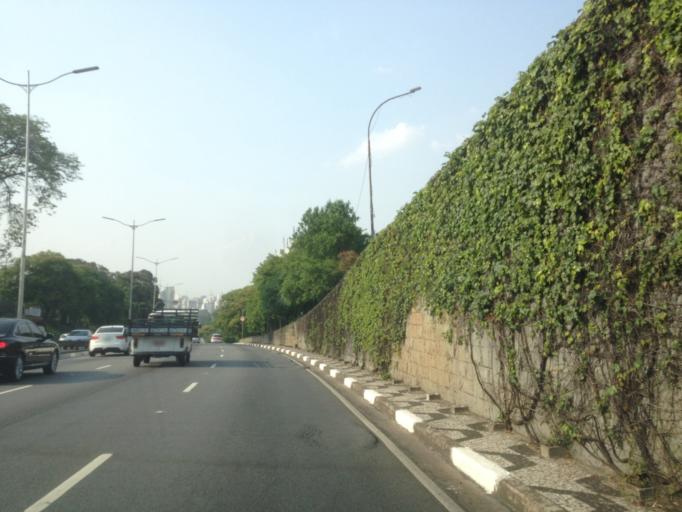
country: BR
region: Sao Paulo
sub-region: Sao Paulo
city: Sao Paulo
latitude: -23.6063
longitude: -46.6516
